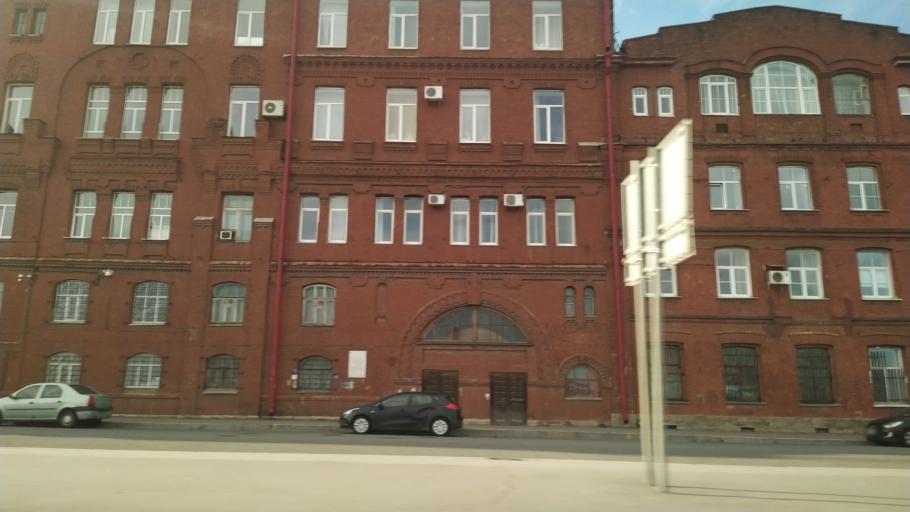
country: RU
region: Leningrad
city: Finlyandskiy
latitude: 59.9598
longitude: 30.3854
